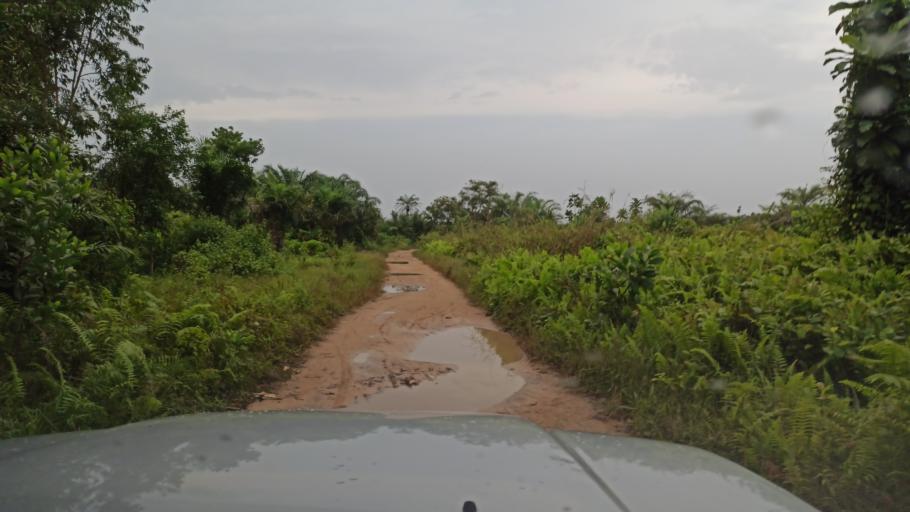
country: BJ
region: Queme
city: Porto-Novo
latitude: 6.4581
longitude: 2.6748
